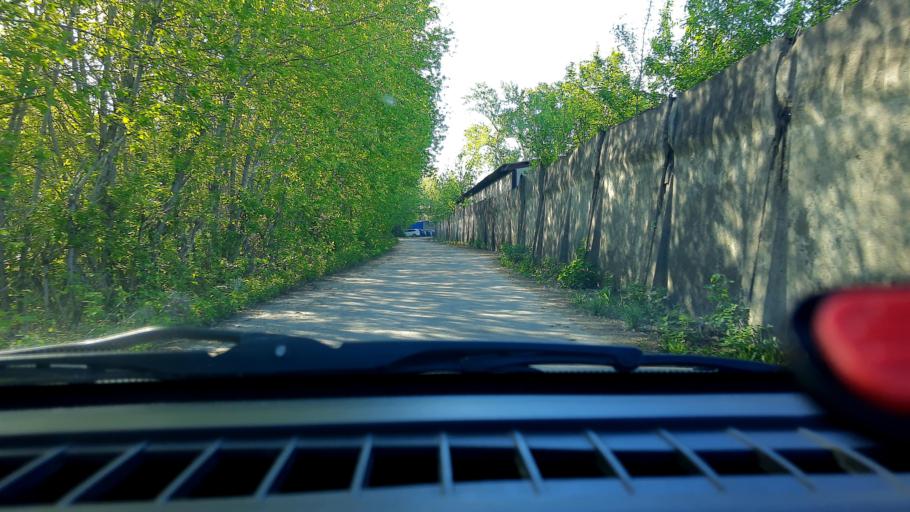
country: RU
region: Nizjnij Novgorod
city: Burevestnik
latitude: 56.2381
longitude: 43.8813
